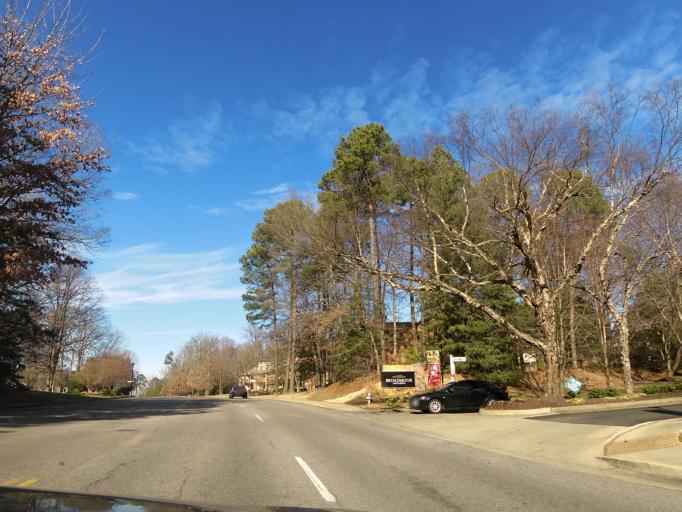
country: US
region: Virginia
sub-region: Henrico County
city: Tuckahoe
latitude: 37.6355
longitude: -77.5603
